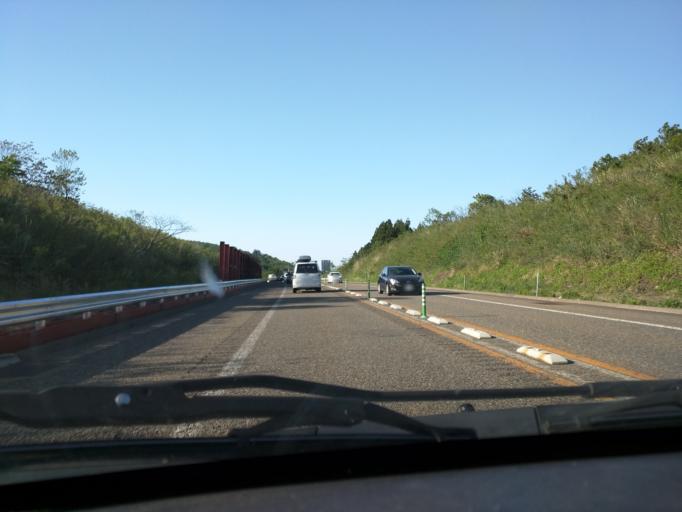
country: JP
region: Niigata
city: Arai
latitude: 37.0359
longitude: 138.2313
